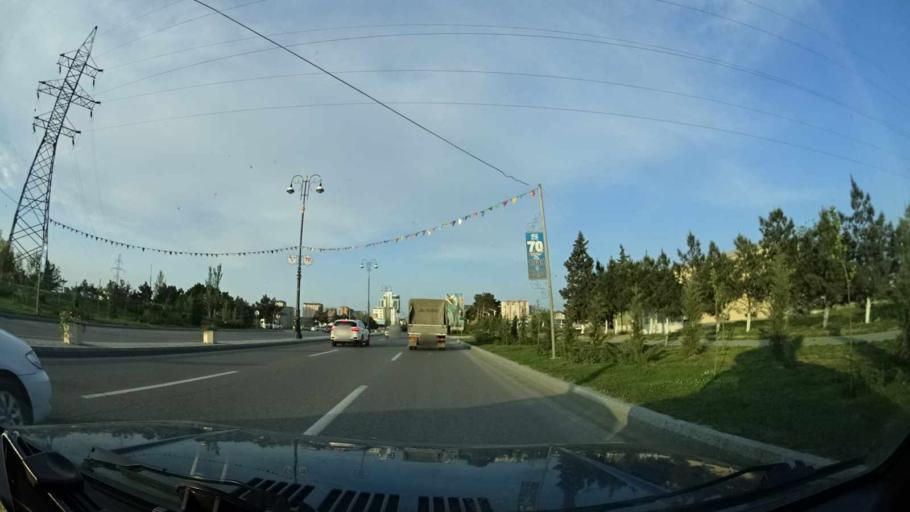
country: AZ
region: Sumqayit
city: Sumqayit
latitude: 40.5824
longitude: 49.6594
